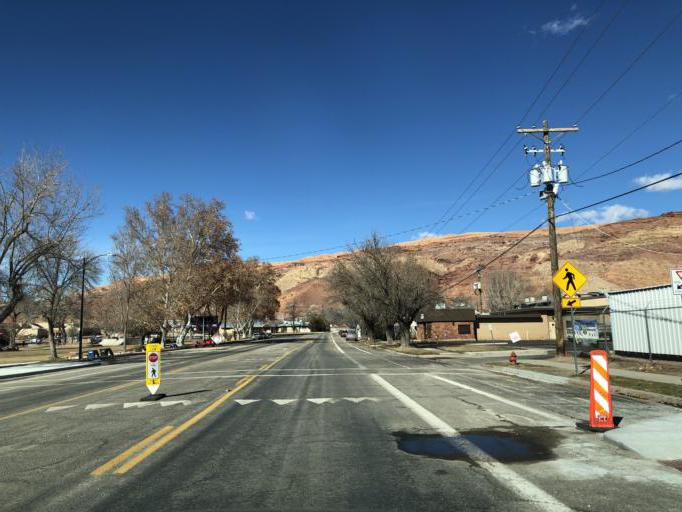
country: US
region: Utah
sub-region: Grand County
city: Moab
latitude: 38.5774
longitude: -109.5527
